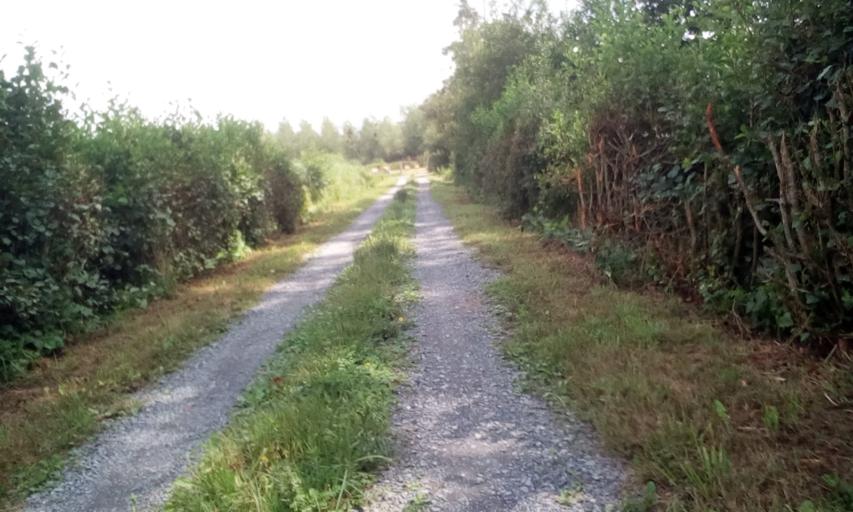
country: FR
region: Lower Normandy
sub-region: Departement du Calvados
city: Bavent
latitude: 49.2381
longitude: -0.1641
